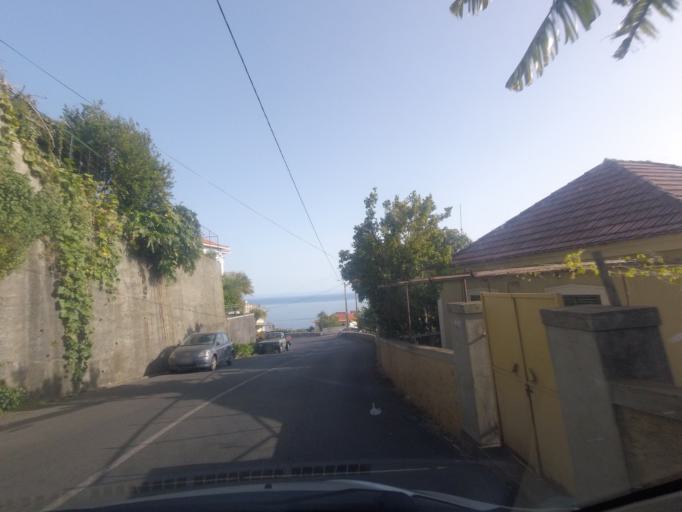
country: PT
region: Madeira
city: Ponta do Sol
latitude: 32.6861
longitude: -17.1068
